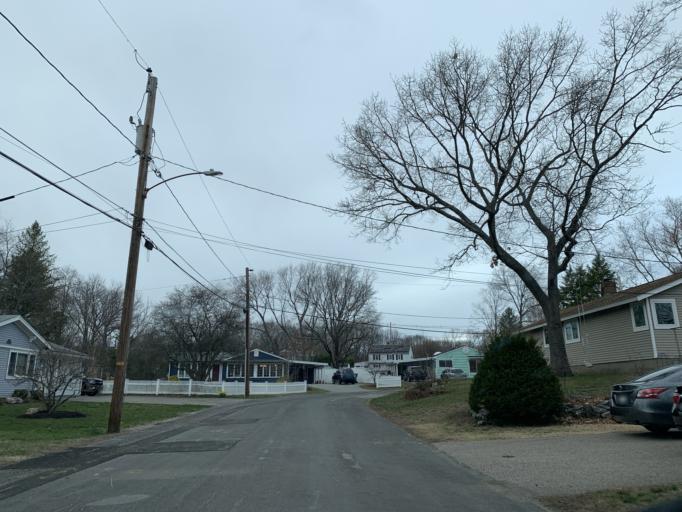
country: US
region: Massachusetts
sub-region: Norfolk County
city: Norwood
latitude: 42.2180
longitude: -71.1841
